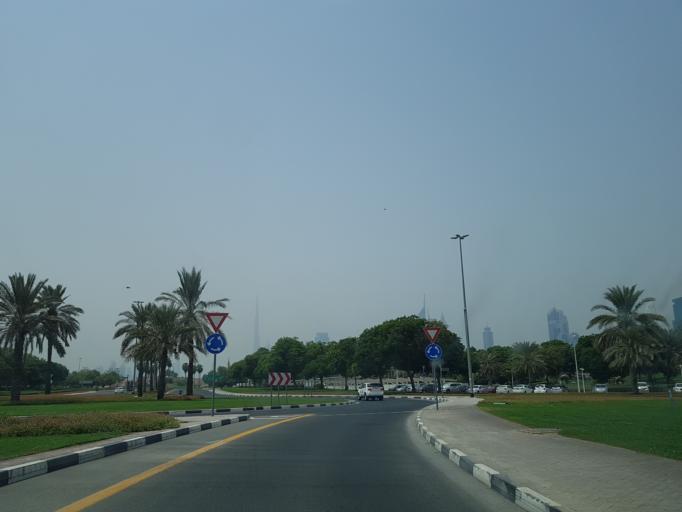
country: AE
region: Ash Shariqah
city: Sharjah
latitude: 25.2285
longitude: 55.3002
